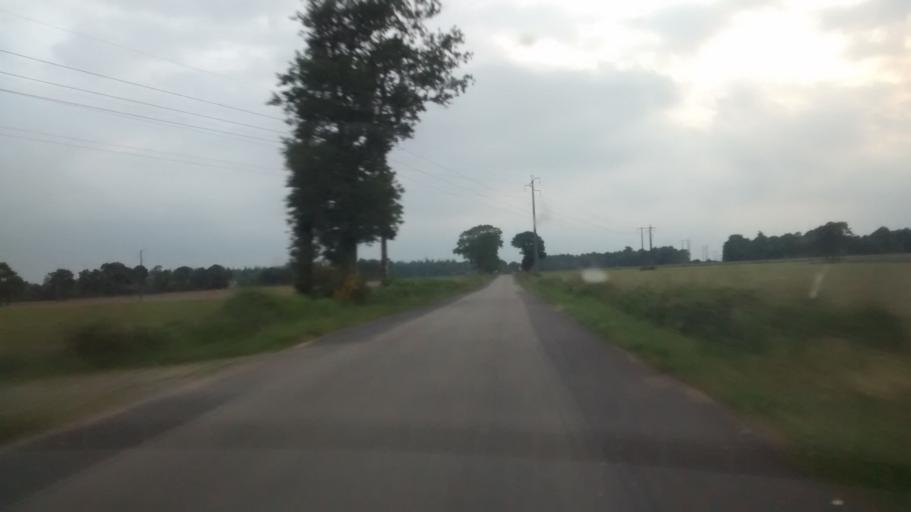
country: FR
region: Brittany
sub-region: Departement du Morbihan
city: Saint-Martin-sur-Oust
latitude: 47.7310
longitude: -2.3029
